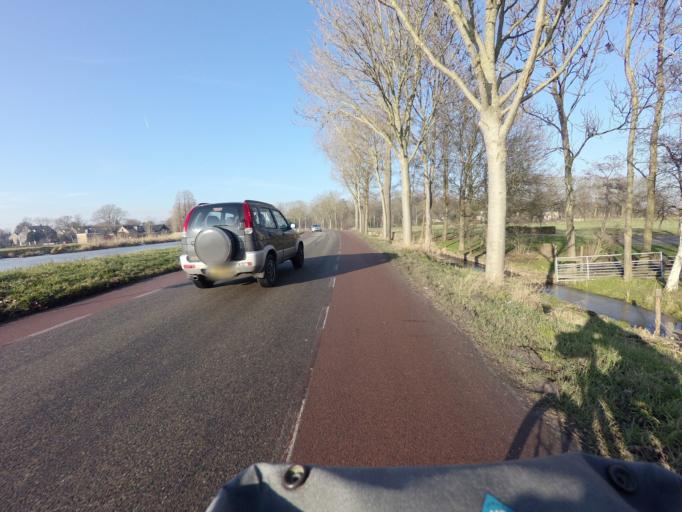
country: NL
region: North Holland
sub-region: Gemeente Amsterdam
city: Amsterdam-Zuidoost
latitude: 52.2674
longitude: 4.9817
